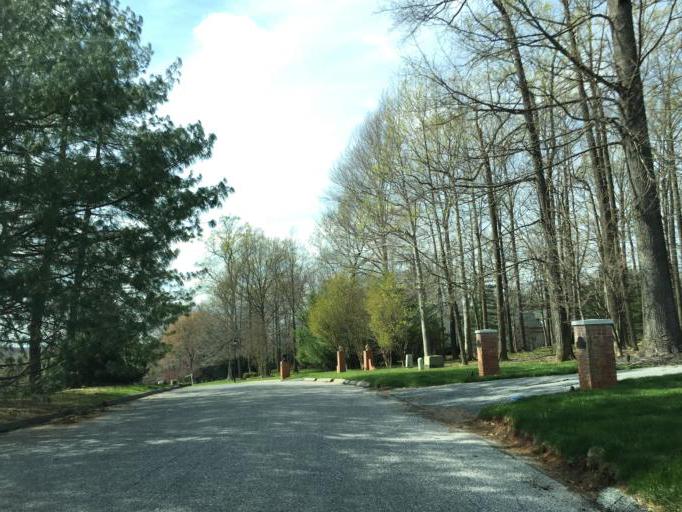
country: US
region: Maryland
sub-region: Baltimore County
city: Cockeysville
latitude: 39.4719
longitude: -76.6735
